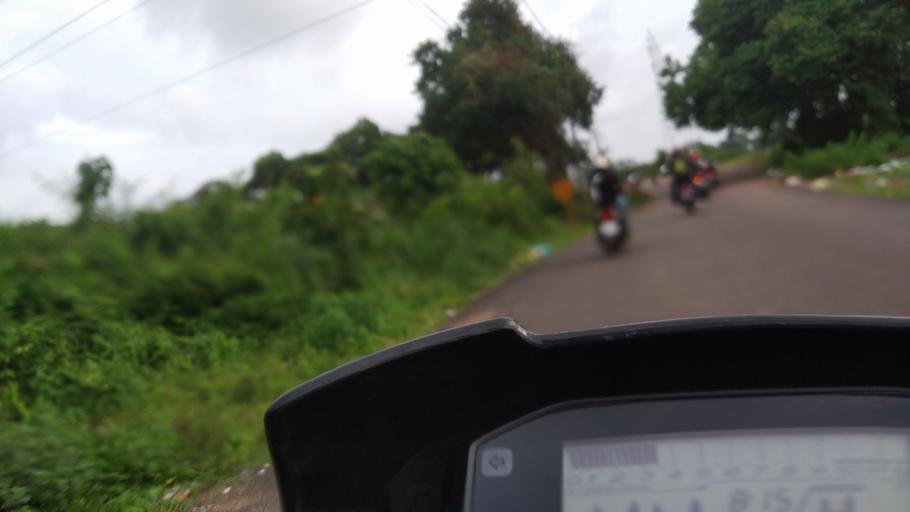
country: IN
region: Kerala
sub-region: Ernakulam
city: Aluva
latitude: 10.0517
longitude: 76.3444
